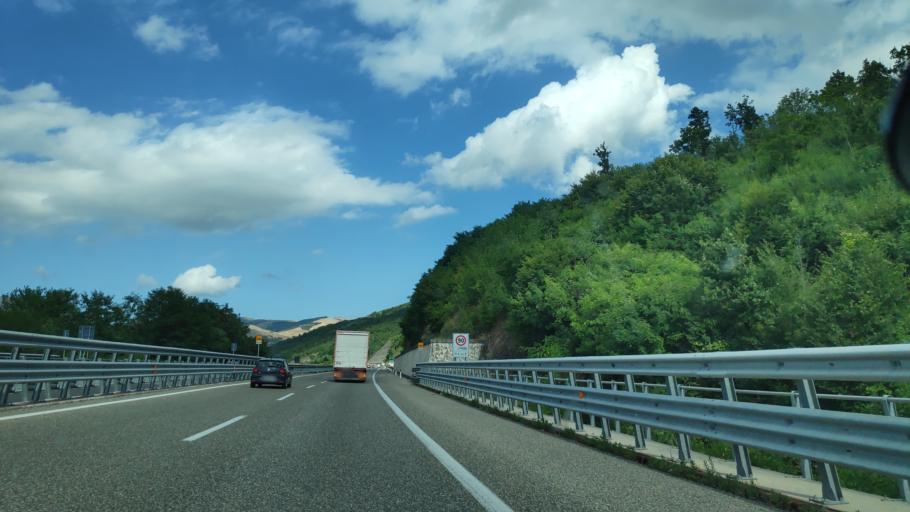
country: IT
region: Campania
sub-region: Provincia di Salerno
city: Pertosa
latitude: 40.5315
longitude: 15.4428
